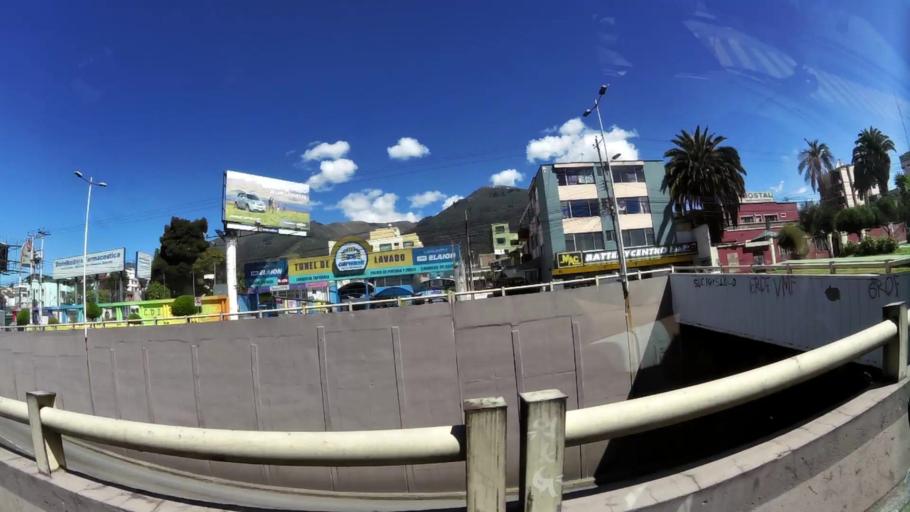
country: EC
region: Pichincha
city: Quito
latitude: -0.1773
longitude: -78.4940
